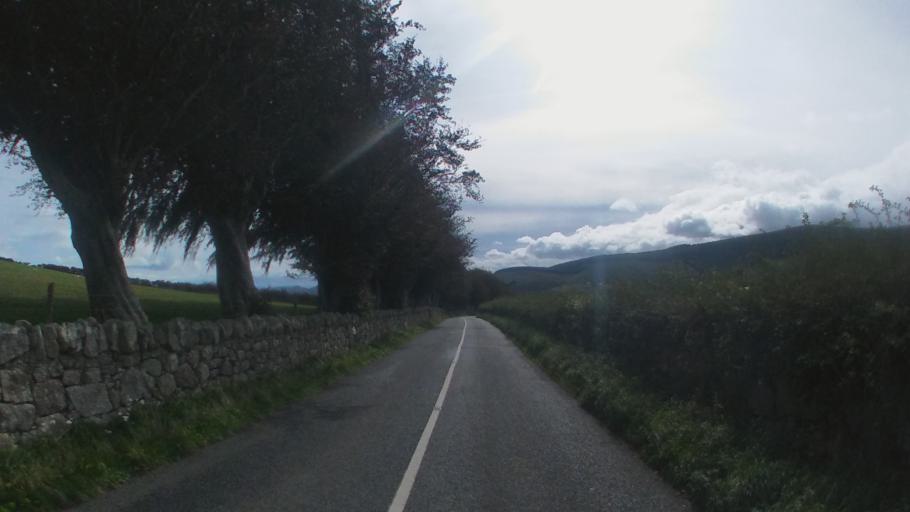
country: IE
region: Leinster
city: Sandyford
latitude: 53.2267
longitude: -6.2209
